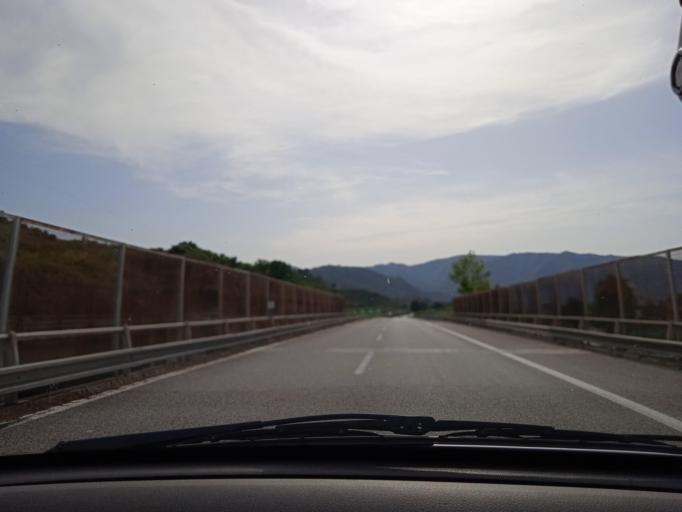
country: IT
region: Sicily
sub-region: Messina
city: Tonnarella
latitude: 38.1143
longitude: 15.0985
